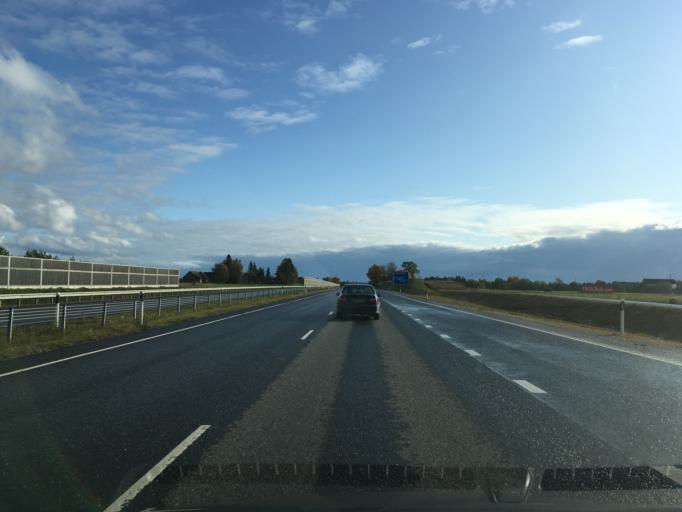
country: EE
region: Harju
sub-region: Rae vald
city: Vaida
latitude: 59.1830
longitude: 25.0877
